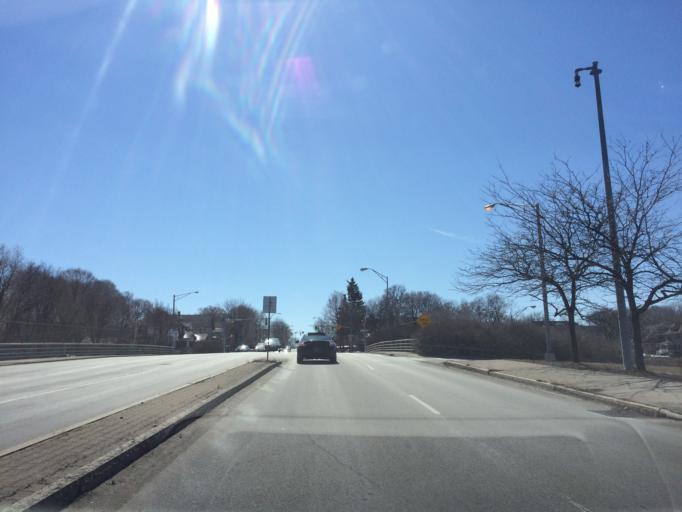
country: US
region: New York
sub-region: Monroe County
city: Brighton
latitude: 43.1453
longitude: -77.5554
